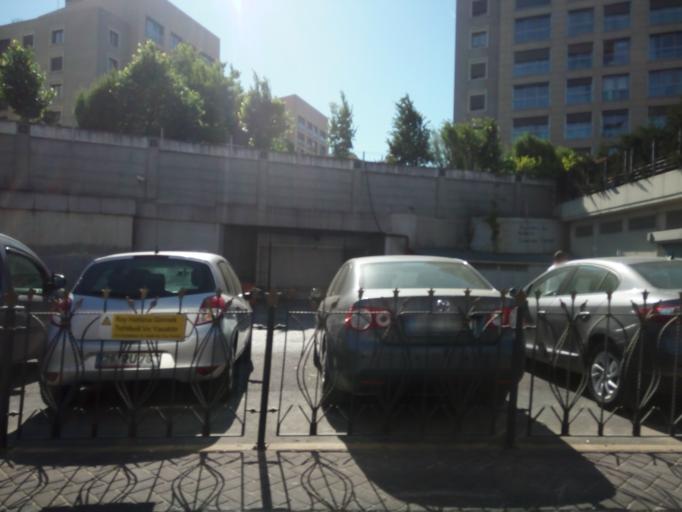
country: TR
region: Istanbul
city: Zeytinburnu
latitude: 41.0106
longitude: 28.9093
